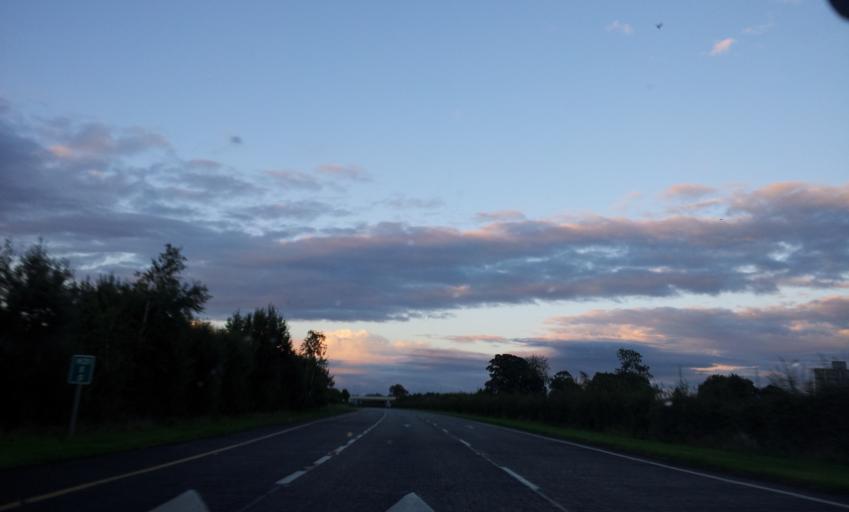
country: IE
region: Munster
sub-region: County Limerick
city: Croom
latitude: 52.5826
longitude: -8.7288
